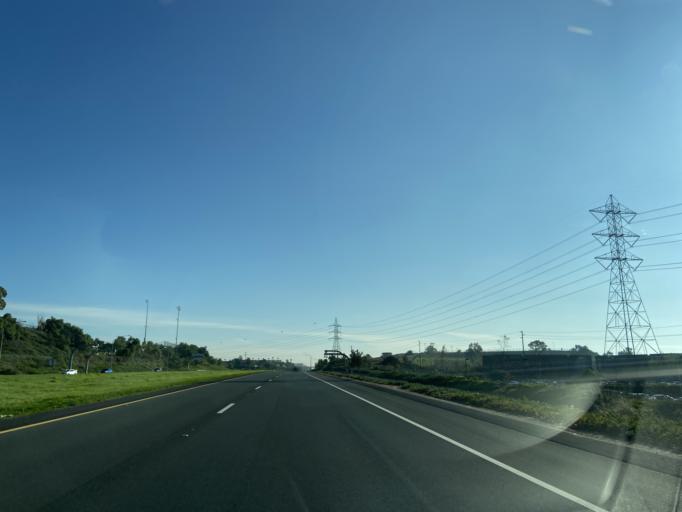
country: US
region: California
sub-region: San Diego County
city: Bonita
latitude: 32.6441
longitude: -116.9710
